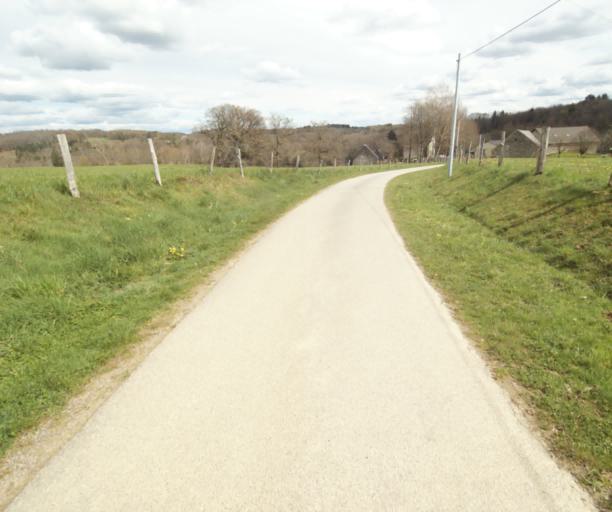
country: FR
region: Limousin
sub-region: Departement de la Correze
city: Laguenne
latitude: 45.2326
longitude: 1.8810
